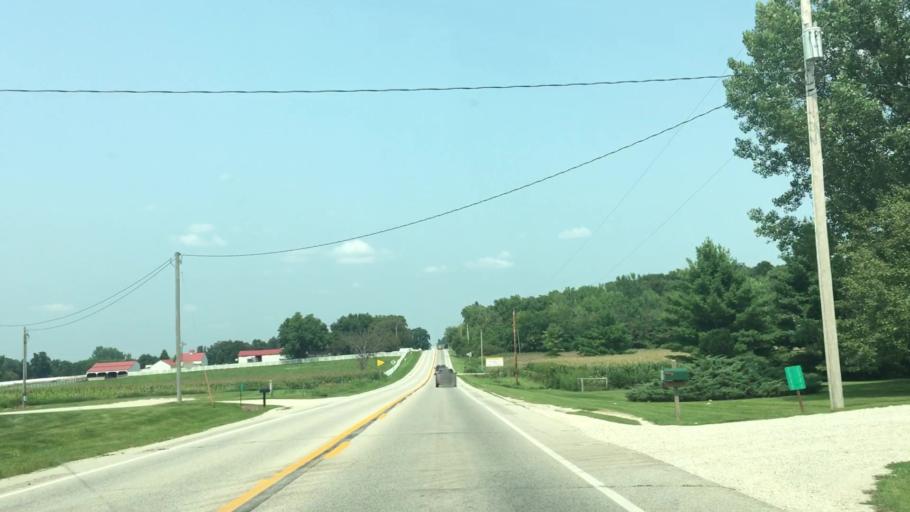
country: US
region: Iowa
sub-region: Buchanan County
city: Independence
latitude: 42.4907
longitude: -91.8895
